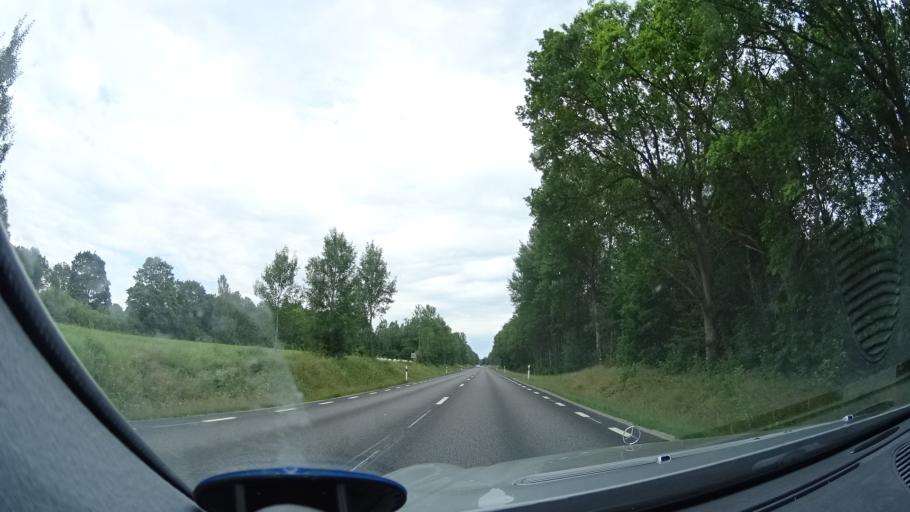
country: SE
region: Kronoberg
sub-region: Tingsryds Kommun
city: Tingsryd
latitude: 56.4876
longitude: 15.0007
